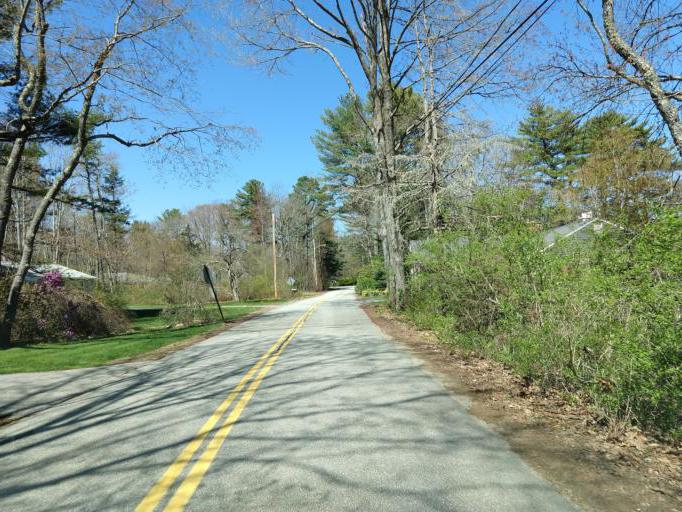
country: US
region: Maine
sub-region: York County
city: Kennebunk
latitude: 43.3459
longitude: -70.5525
